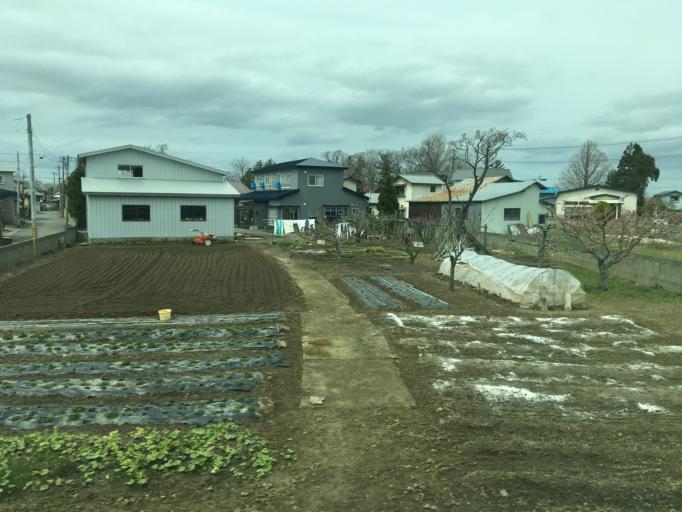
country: JP
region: Aomori
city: Shimokizukuri
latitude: 40.7959
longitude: 140.3778
